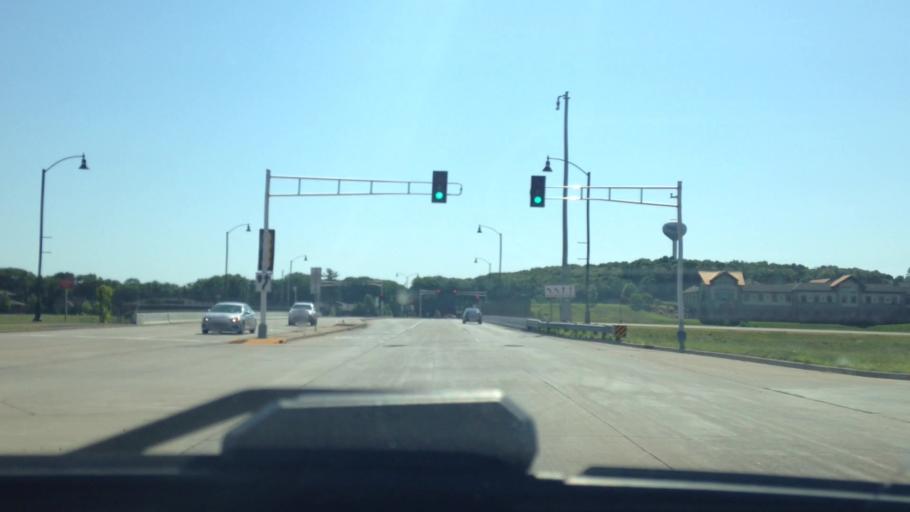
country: US
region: Wisconsin
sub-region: Eau Claire County
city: Altoona
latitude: 44.8179
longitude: -91.4558
